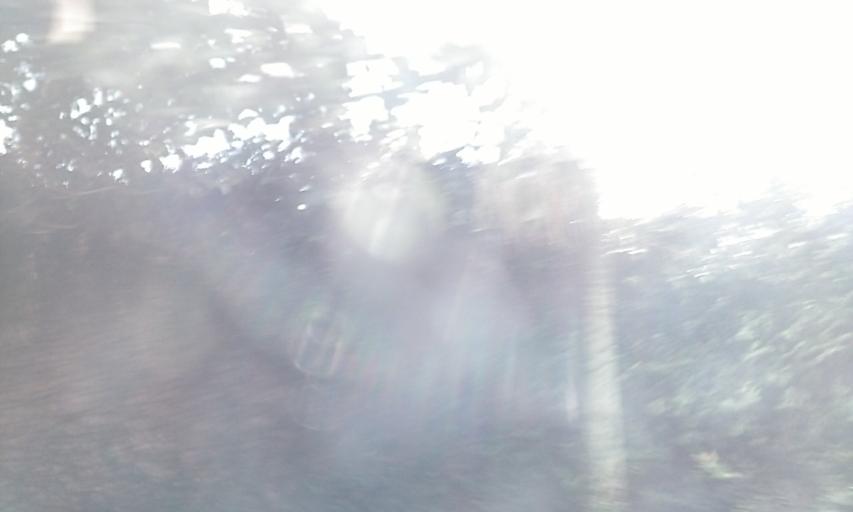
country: UG
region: Central Region
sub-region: Kampala District
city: Kampala
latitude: 0.3297
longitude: 32.5988
